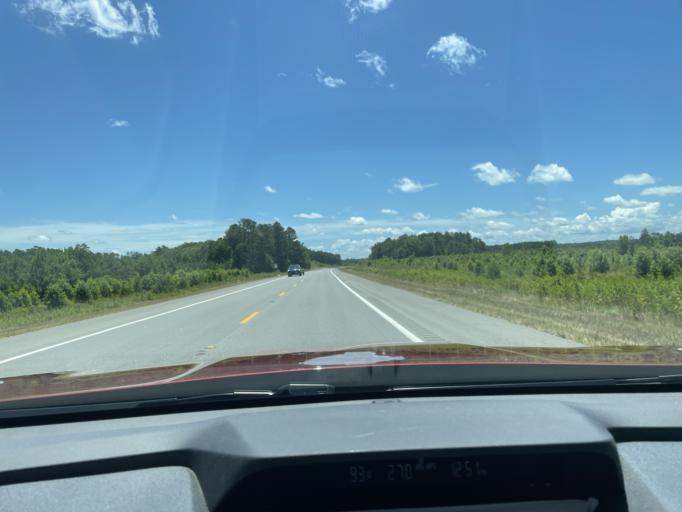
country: US
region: Arkansas
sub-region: Lincoln County
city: Star City
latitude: 33.9358
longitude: -91.8914
